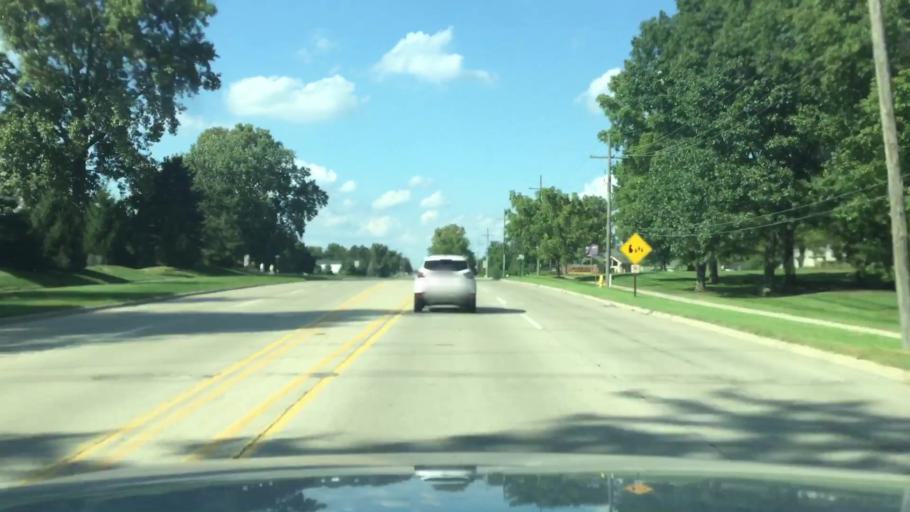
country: US
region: Michigan
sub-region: Wayne County
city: Westland
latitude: 42.3398
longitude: -83.4094
